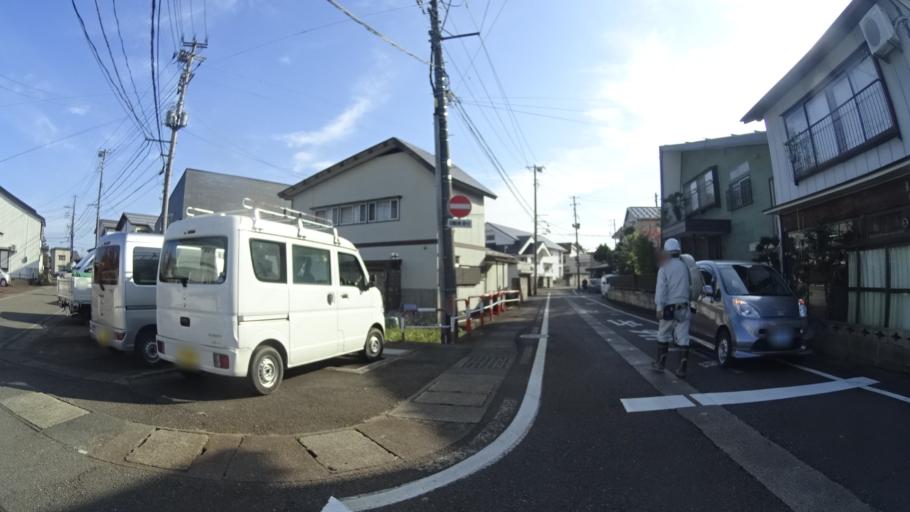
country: JP
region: Niigata
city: Joetsu
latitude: 37.1058
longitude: 138.2450
